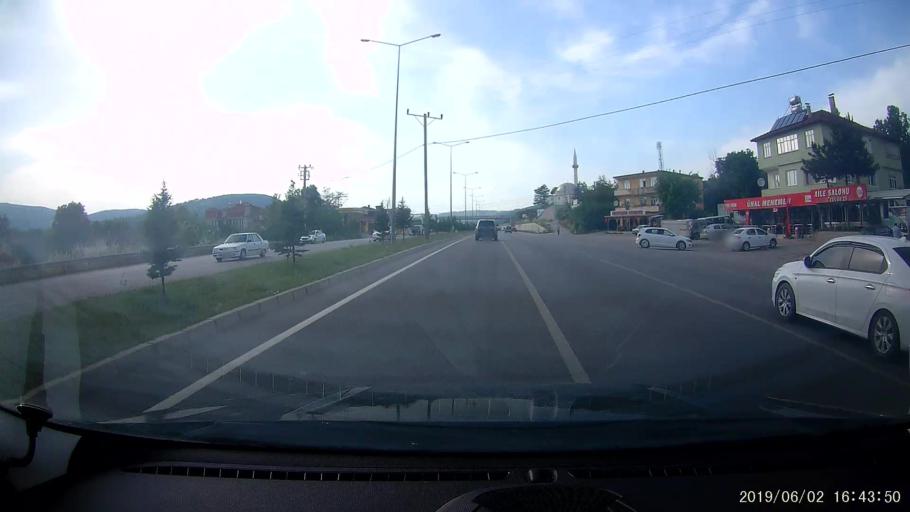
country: TR
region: Samsun
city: Kavak
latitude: 41.1414
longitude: 36.1200
